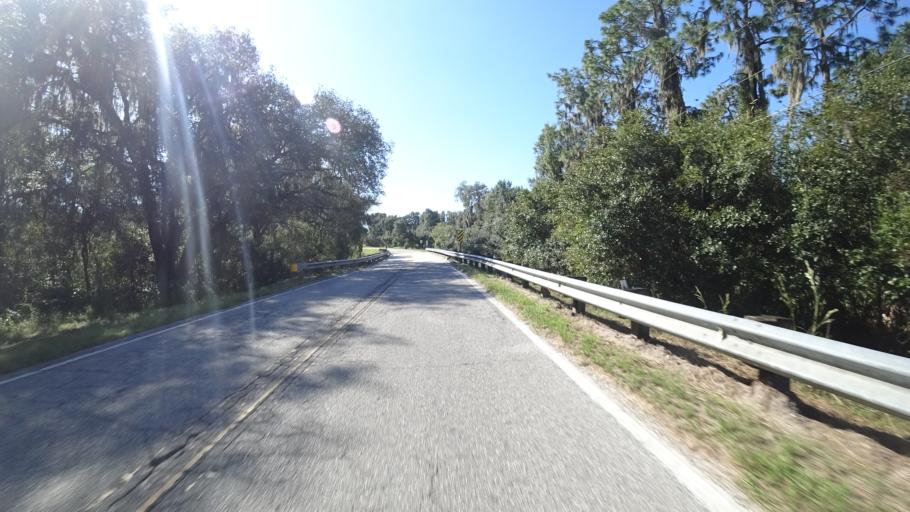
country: US
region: Florida
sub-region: Hillsborough County
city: Wimauma
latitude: 27.6499
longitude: -82.2944
